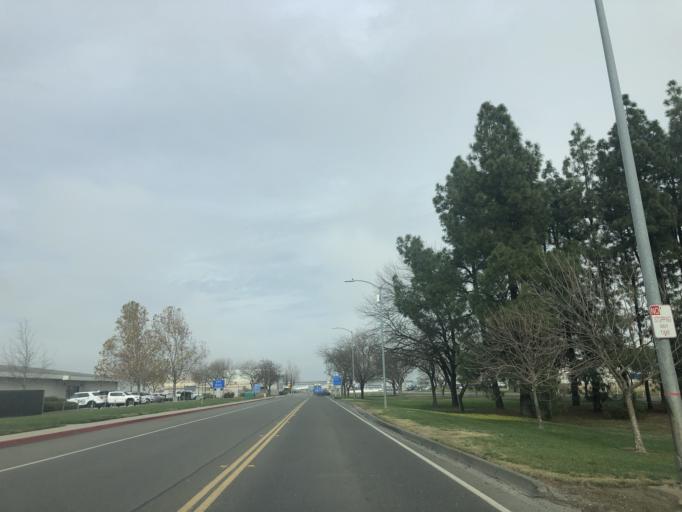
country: US
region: California
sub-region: Yolo County
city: West Sacramento
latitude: 38.6883
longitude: -121.5947
